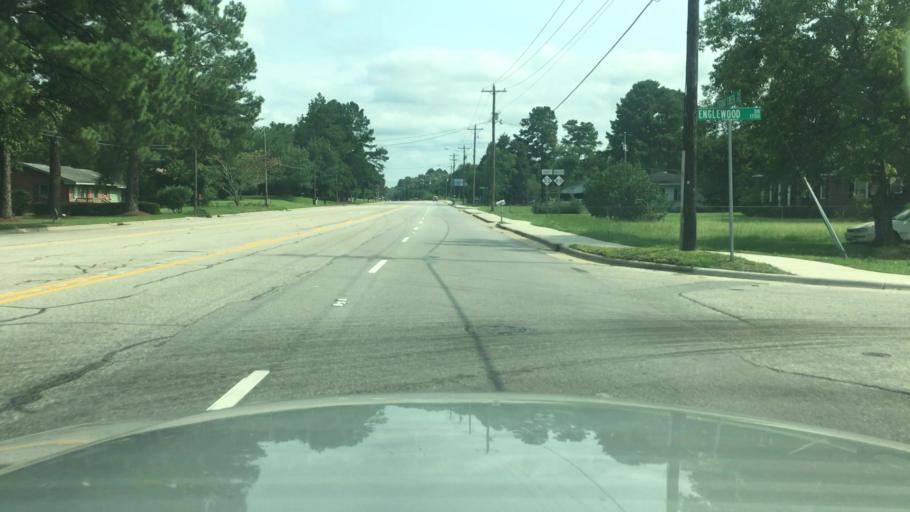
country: US
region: North Carolina
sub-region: Cumberland County
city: Fayetteville
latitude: 35.0269
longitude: -78.8431
